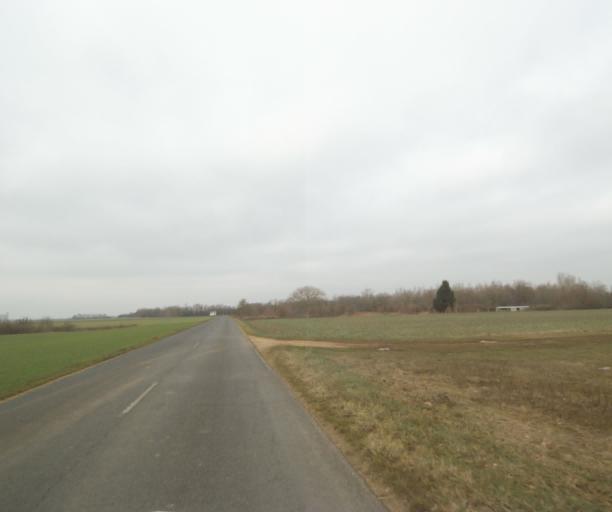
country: FR
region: Champagne-Ardenne
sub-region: Departement de la Haute-Marne
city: Villiers-en-Lieu
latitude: 48.6524
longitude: 4.8014
